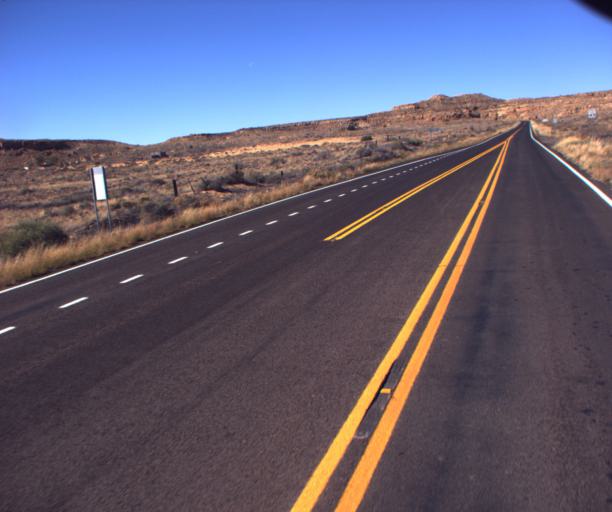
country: US
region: Arizona
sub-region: Navajo County
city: First Mesa
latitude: 35.8798
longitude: -110.6134
